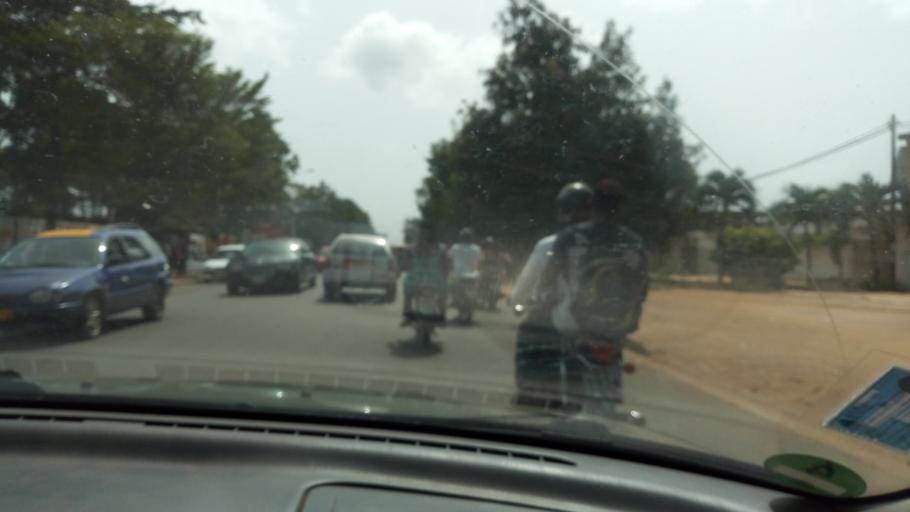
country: TG
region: Maritime
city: Lome
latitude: 6.1722
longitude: 1.1887
